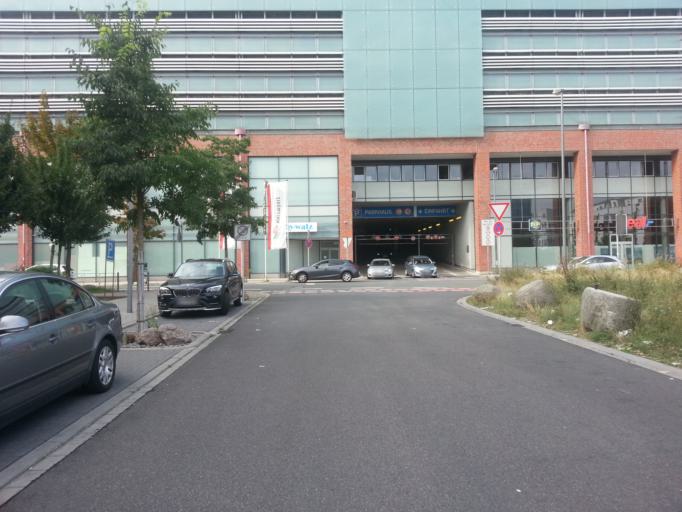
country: DE
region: Rheinland-Pfalz
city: Ludwigshafen am Rhein
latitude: 49.4778
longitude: 8.4543
